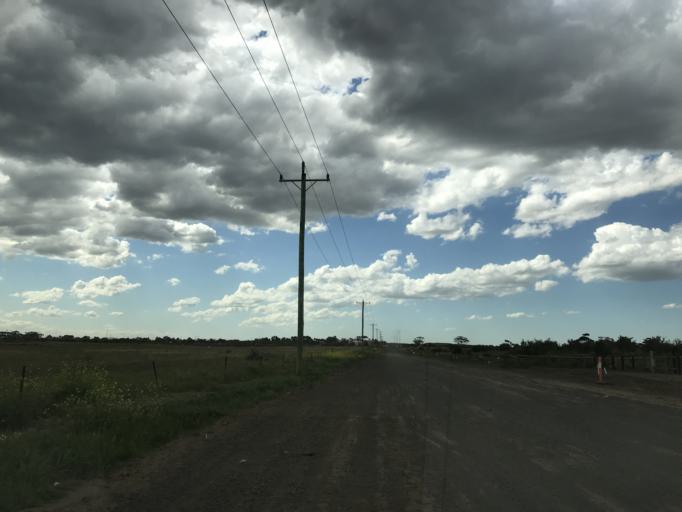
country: AU
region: Victoria
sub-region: Wyndham
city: Truganina
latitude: -37.8185
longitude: 144.7220
